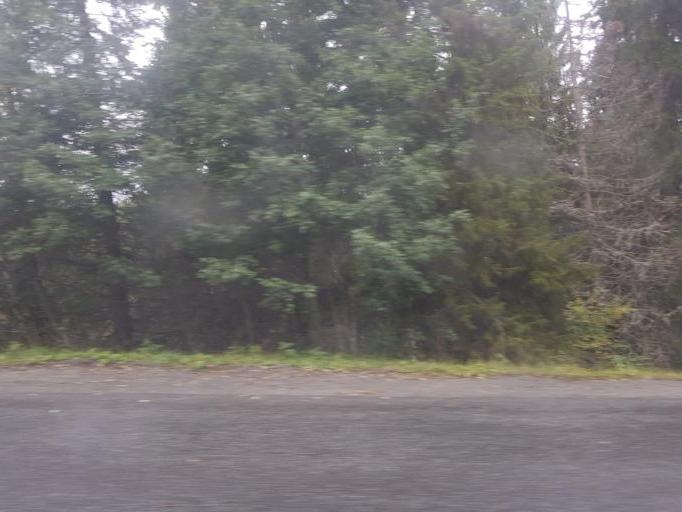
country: NO
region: Sor-Trondelag
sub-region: Trondheim
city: Trondheim
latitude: 63.4159
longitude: 10.3083
